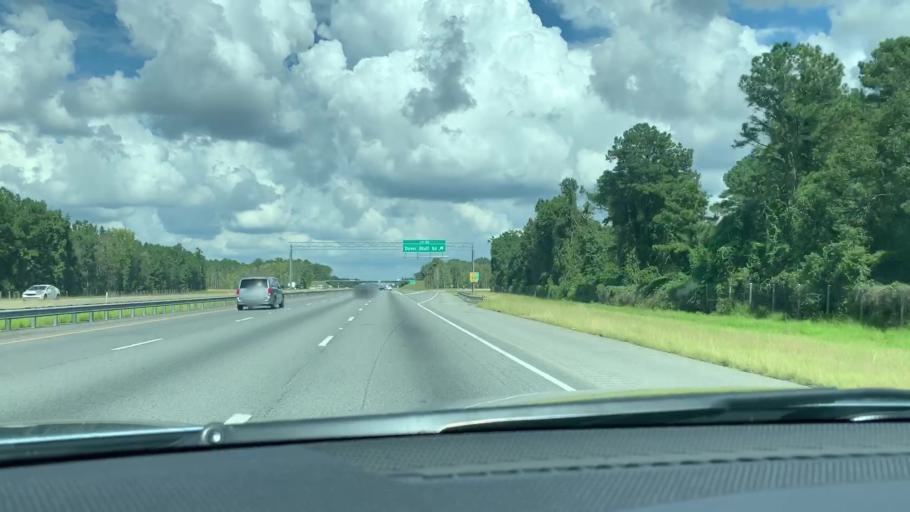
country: US
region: Georgia
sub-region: Glynn County
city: Brunswick
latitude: 31.0962
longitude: -81.6013
